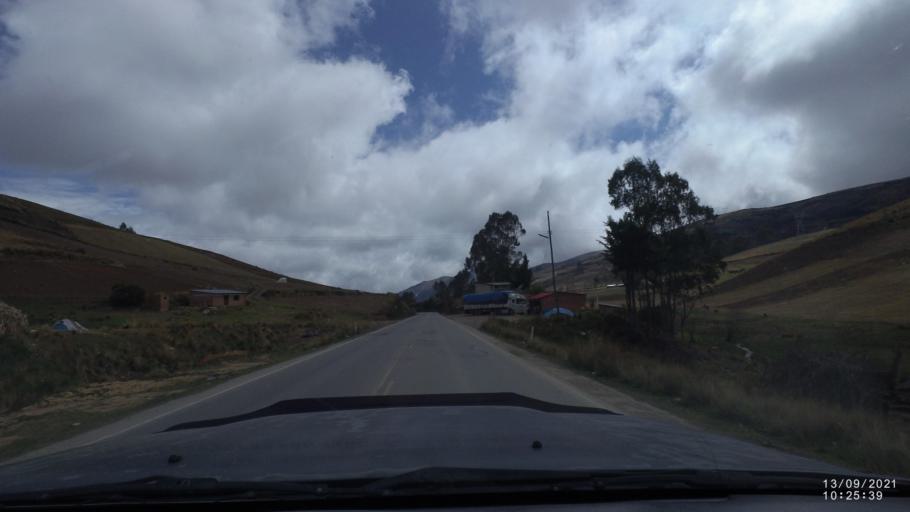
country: BO
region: Cochabamba
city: Colomi
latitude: -17.3094
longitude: -65.8660
